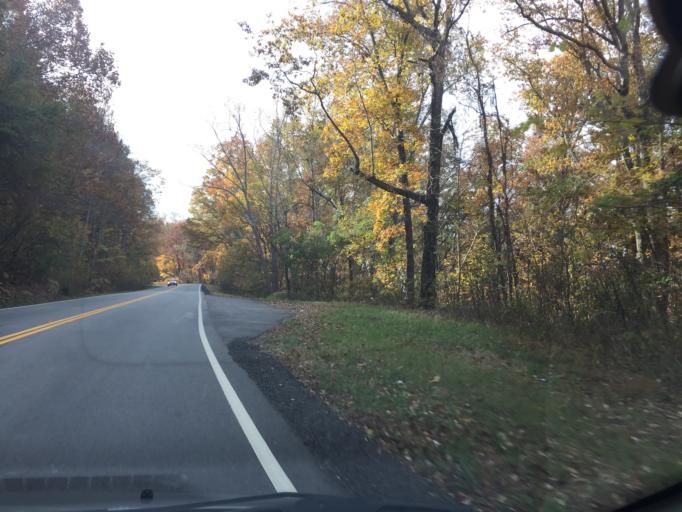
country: US
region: Georgia
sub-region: Dade County
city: Trenton
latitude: 34.8473
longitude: -85.4993
